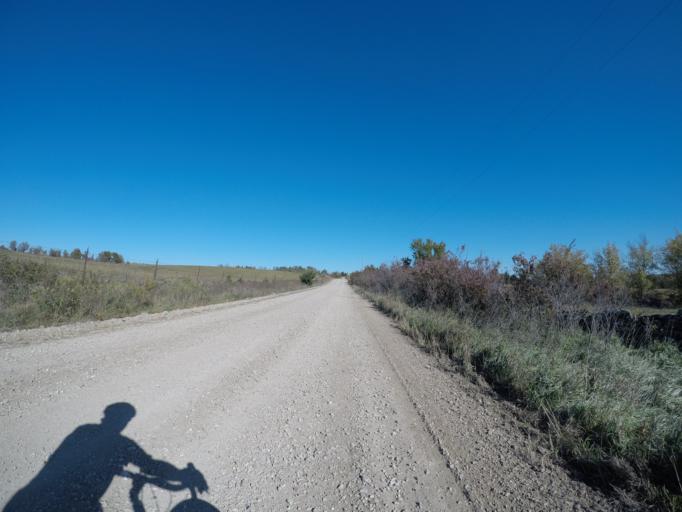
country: US
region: Kansas
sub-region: Wabaunsee County
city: Alma
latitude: 38.9087
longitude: -96.3628
